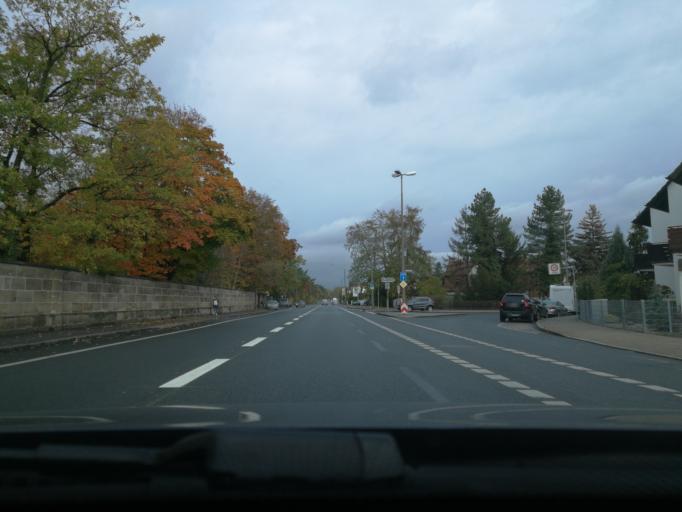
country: DE
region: Bavaria
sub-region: Regierungsbezirk Mittelfranken
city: Furth
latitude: 49.4878
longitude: 10.9946
